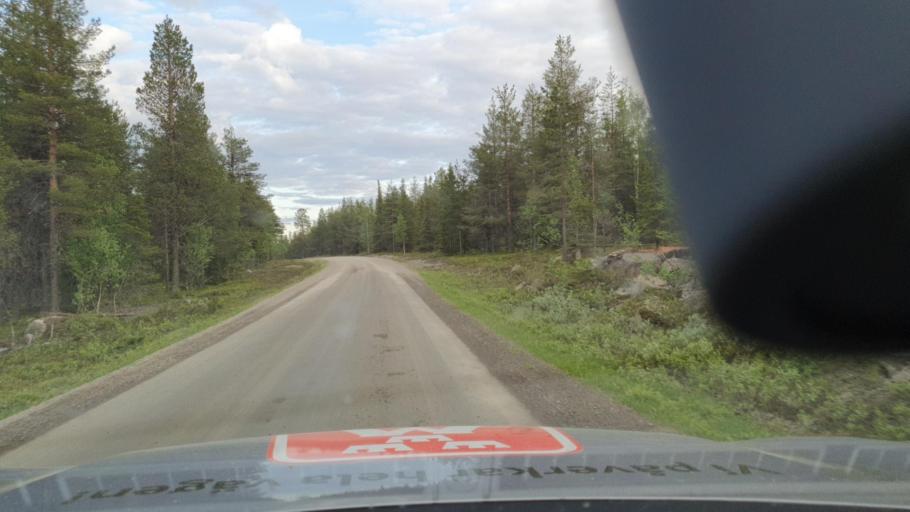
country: SE
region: Norrbotten
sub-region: Gallivare Kommun
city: Gaellivare
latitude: 66.7072
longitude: 21.1561
